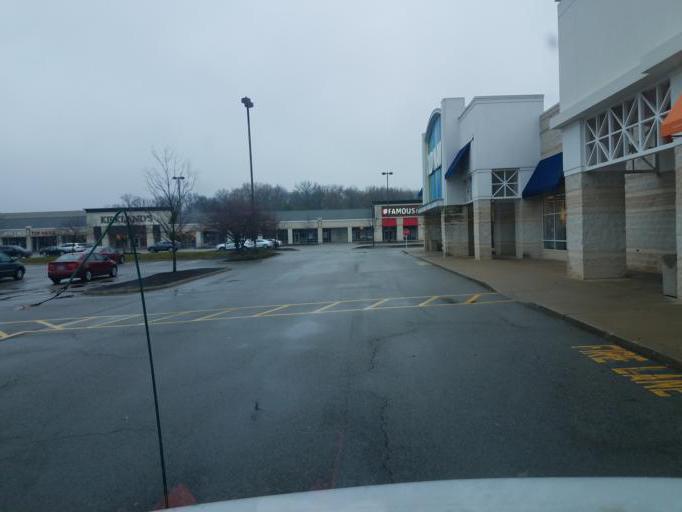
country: US
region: Ohio
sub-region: Franklin County
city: Dublin
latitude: 40.0972
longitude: -83.0854
